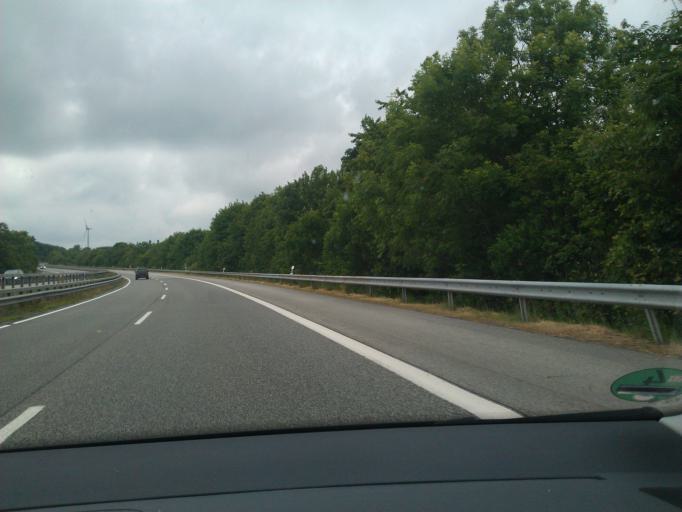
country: DE
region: Rheinland-Pfalz
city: Ruckweiler
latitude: 49.5745
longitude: 7.2446
